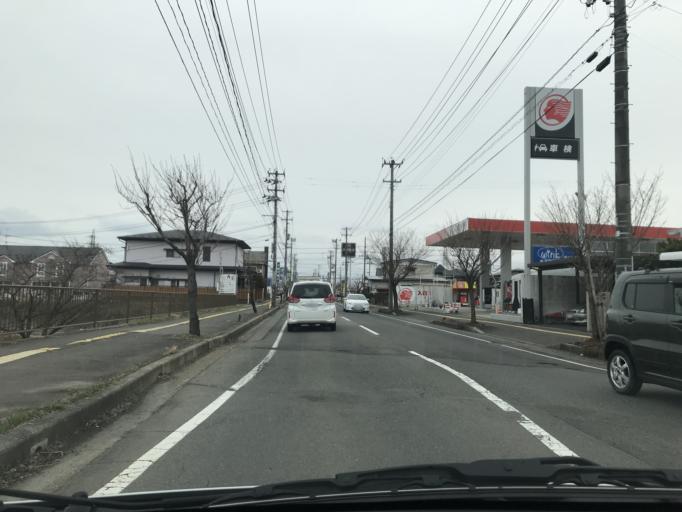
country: JP
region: Iwate
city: Hanamaki
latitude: 39.3948
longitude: 141.1073
